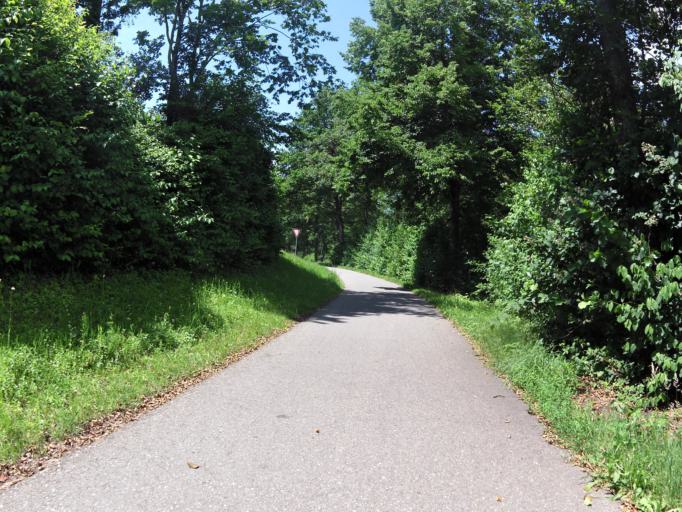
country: DE
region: Baden-Wuerttemberg
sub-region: Freiburg Region
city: Hohberg
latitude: 48.3355
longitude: 7.9115
